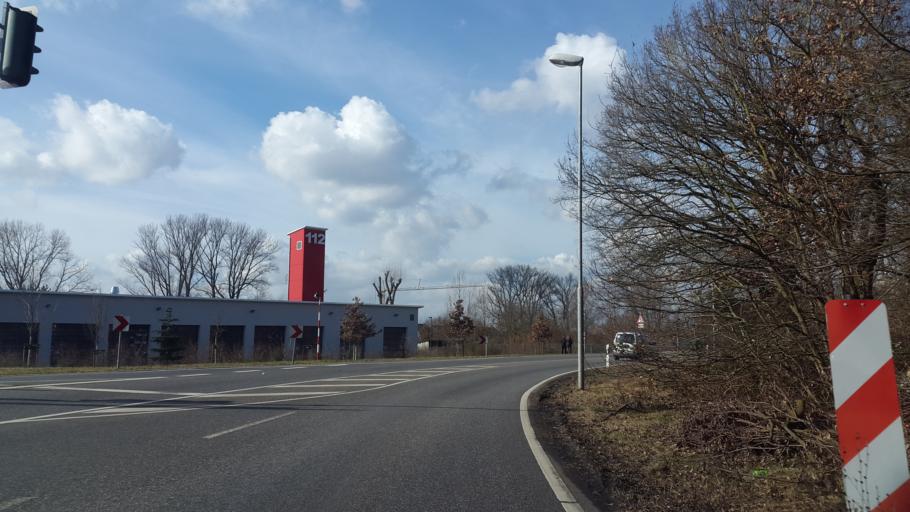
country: DE
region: Hesse
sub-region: Regierungsbezirk Darmstadt
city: Rodgau
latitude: 50.0381
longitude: 8.8855
